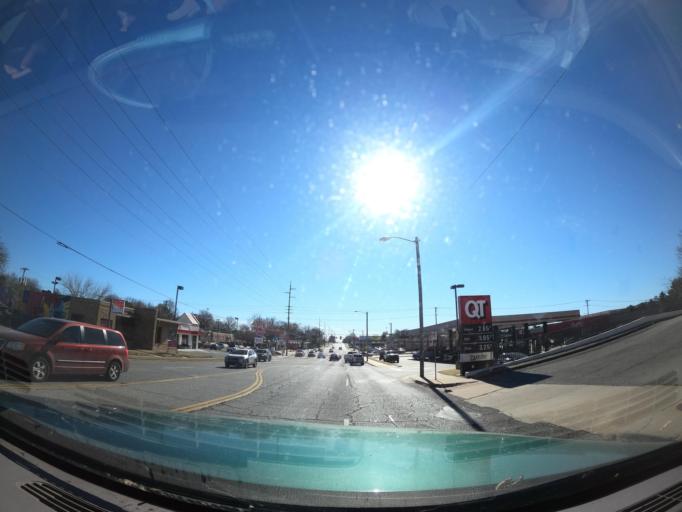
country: US
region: Oklahoma
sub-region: Tulsa County
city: Tulsa
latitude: 36.1341
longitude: -95.9404
